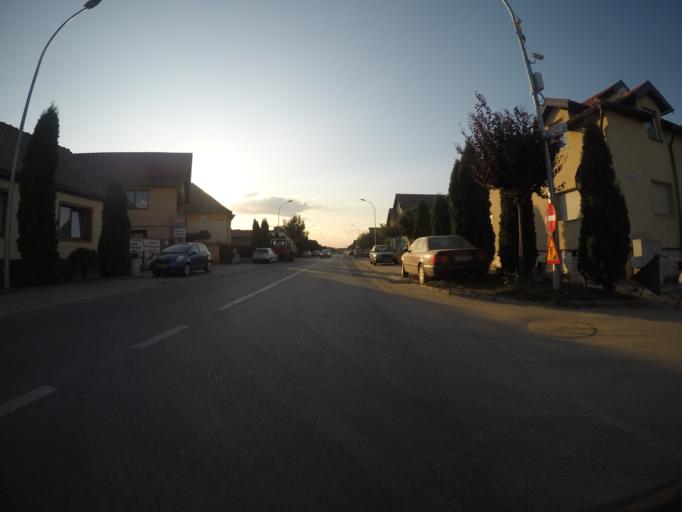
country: RO
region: Sibiu
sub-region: Comuna Selimbar
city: Selimbar
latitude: 45.7702
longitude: 24.1855
